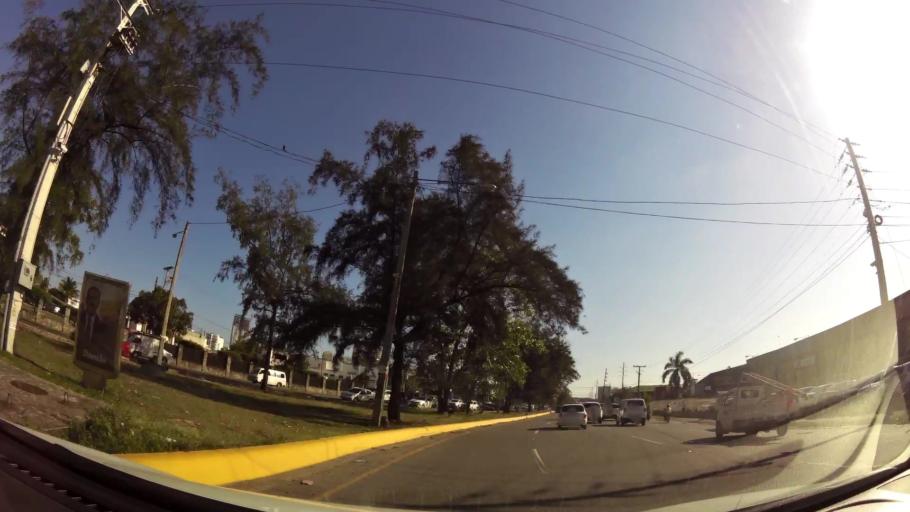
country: DO
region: Nacional
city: Bella Vista
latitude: 18.4482
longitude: -69.9756
